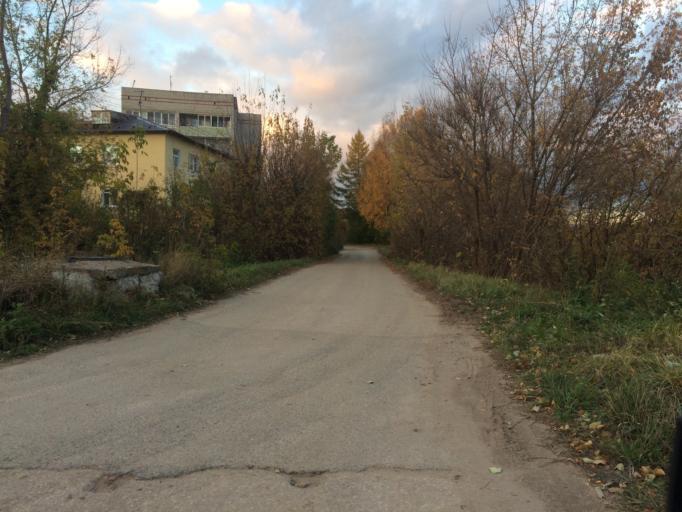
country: RU
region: Mariy-El
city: Yoshkar-Ola
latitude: 56.6176
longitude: 47.9093
